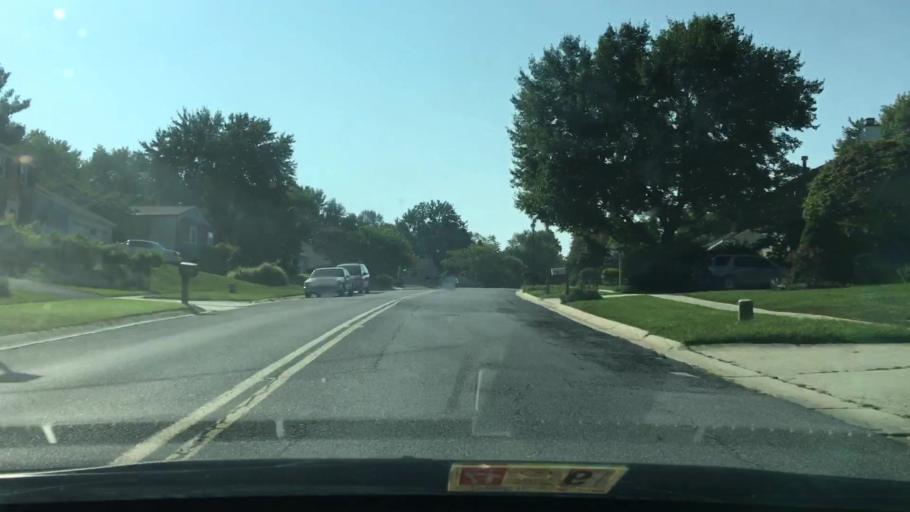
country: US
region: Maryland
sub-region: Montgomery County
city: Damascus
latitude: 39.2599
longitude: -77.2145
